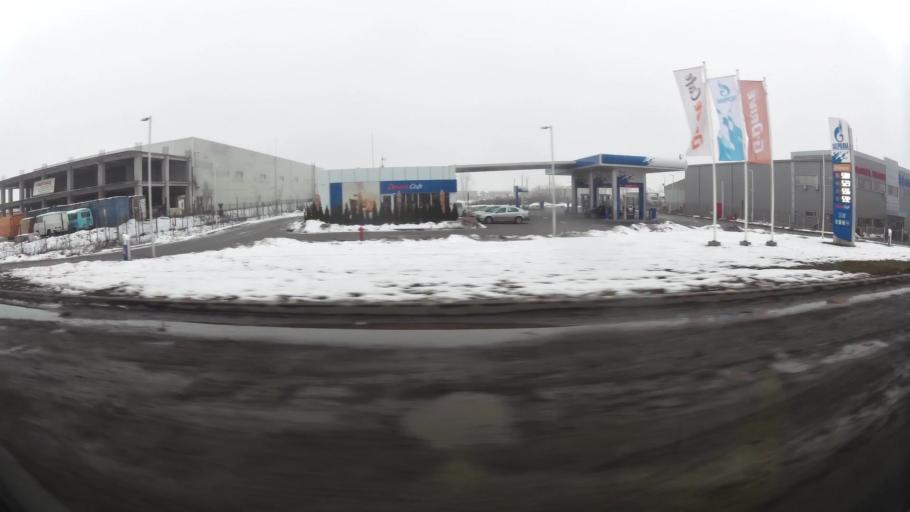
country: RO
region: Ilfov
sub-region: Comuna Bragadiru
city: Bragadiru
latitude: 44.3984
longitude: 25.9807
